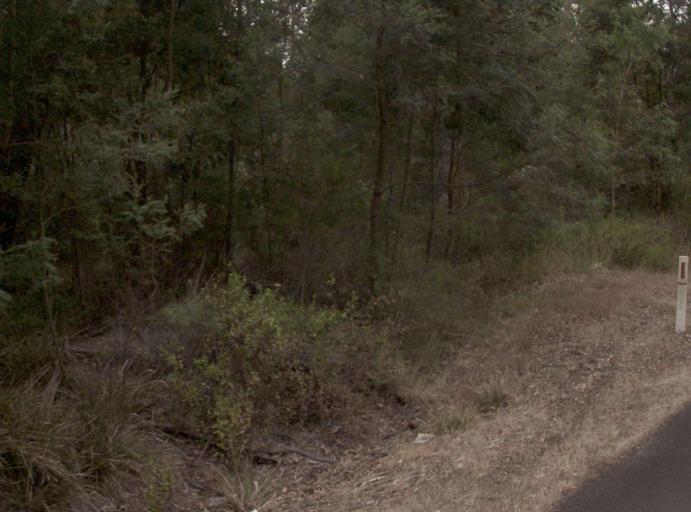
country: AU
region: Victoria
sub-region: Wellington
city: Sale
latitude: -38.4108
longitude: 146.9636
